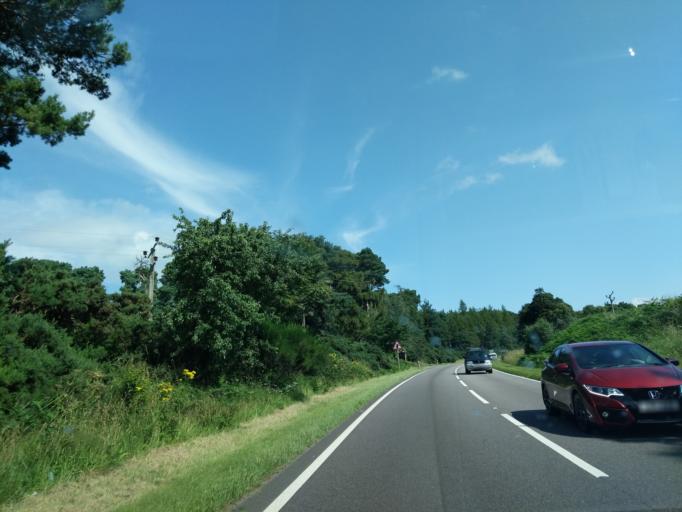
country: GB
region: Scotland
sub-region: Moray
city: Lhanbryd
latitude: 57.6342
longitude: -3.1915
